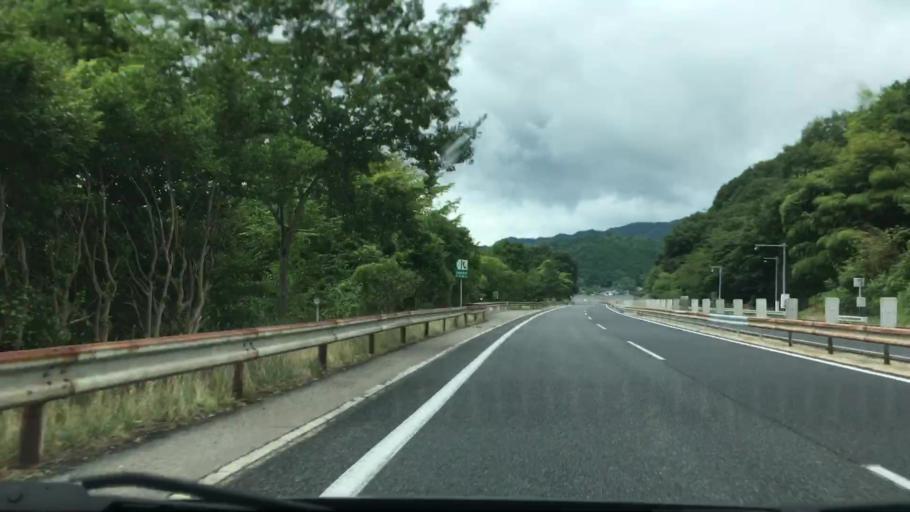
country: JP
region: Okayama
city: Takahashi
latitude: 34.9872
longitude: 133.7041
